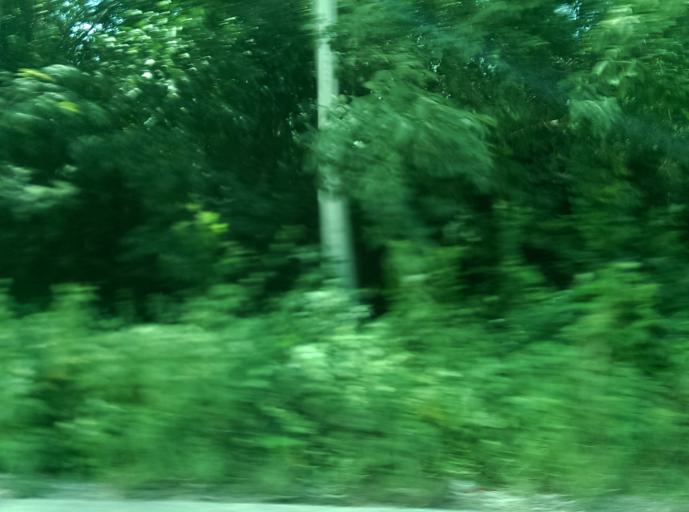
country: MX
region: Quintana Roo
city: Tulum
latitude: 20.2252
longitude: -87.4573
